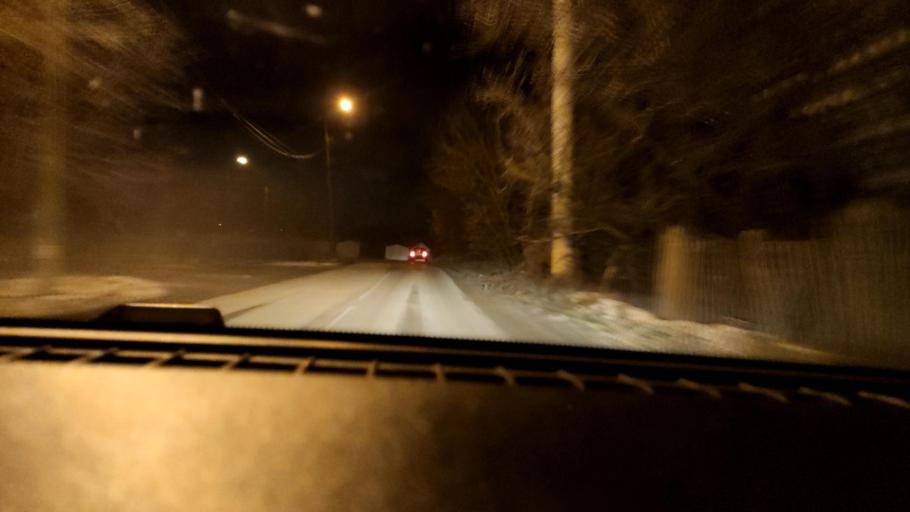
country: RU
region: Samara
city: Samara
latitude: 53.1367
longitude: 50.1216
